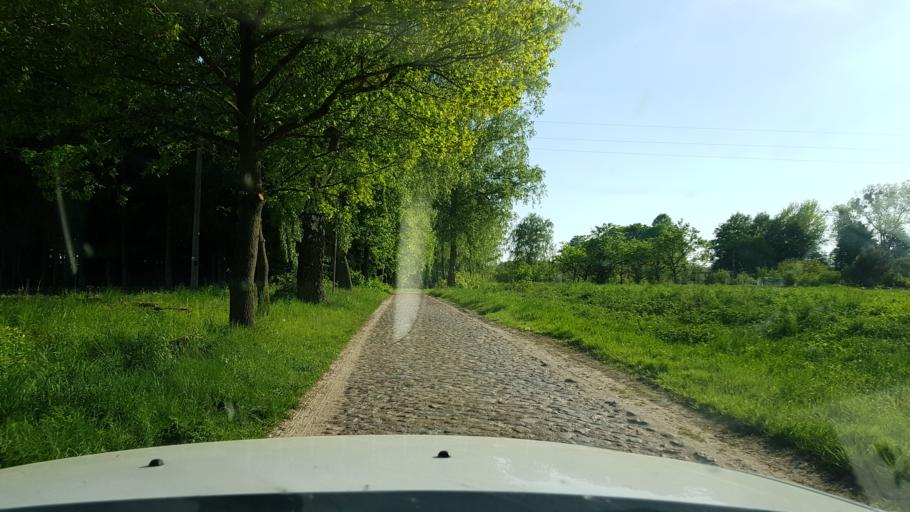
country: PL
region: West Pomeranian Voivodeship
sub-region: Powiat lobeski
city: Resko
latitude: 53.7117
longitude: 15.3360
